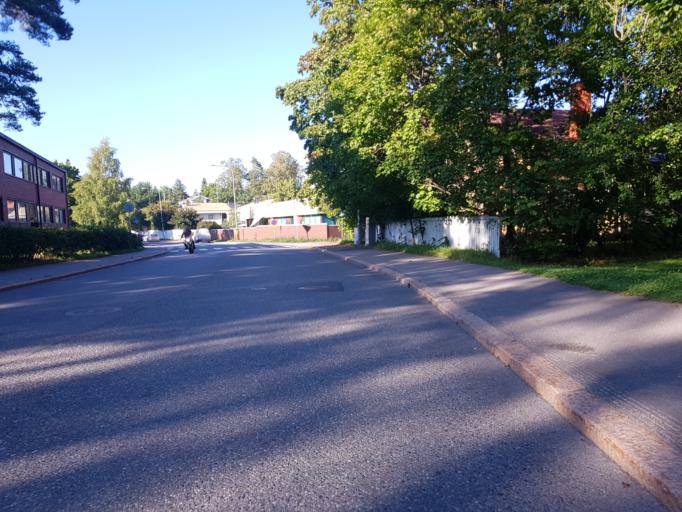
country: FI
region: Uusimaa
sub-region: Helsinki
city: Helsinki
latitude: 60.2253
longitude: 24.9733
